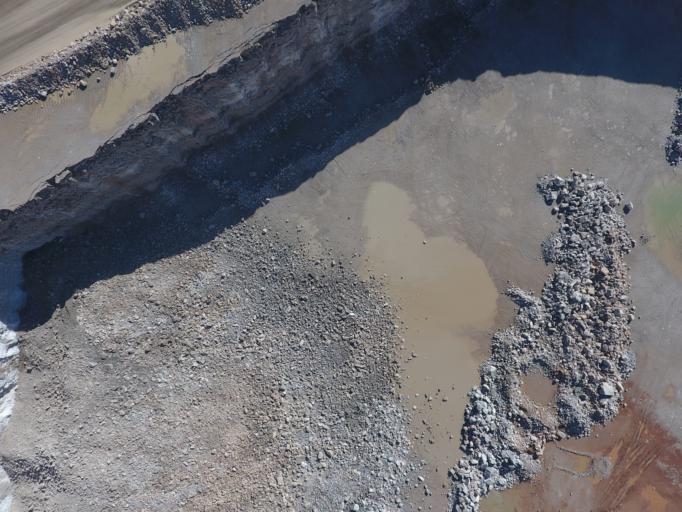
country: US
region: Texas
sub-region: Wise County
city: Chico
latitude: 33.2784
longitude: -97.8232
